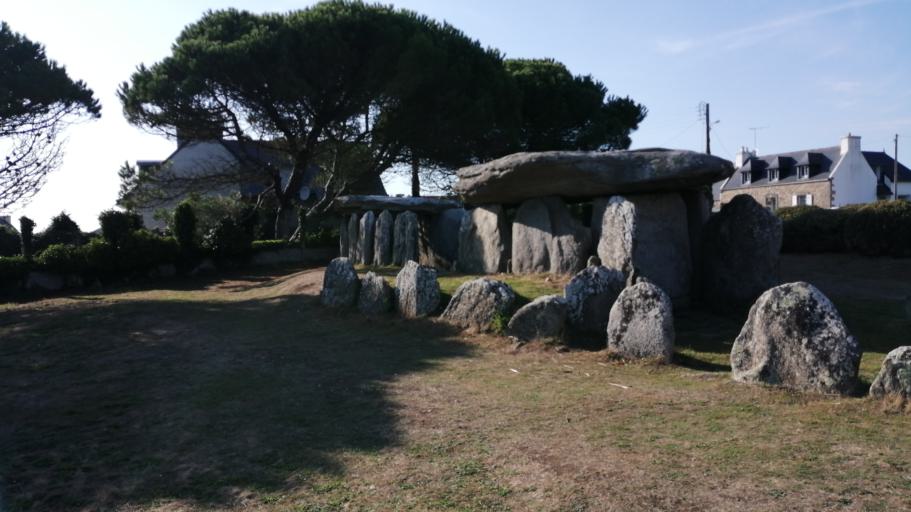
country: FR
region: Brittany
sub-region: Departement du Finistere
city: Plouhinec
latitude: 47.9862
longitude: -4.4655
